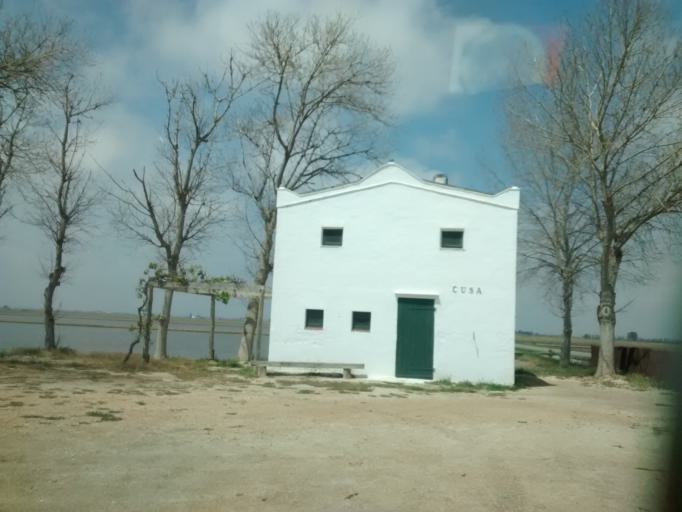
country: ES
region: Catalonia
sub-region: Provincia de Tarragona
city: Deltebre
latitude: 40.6781
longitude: 0.7989
